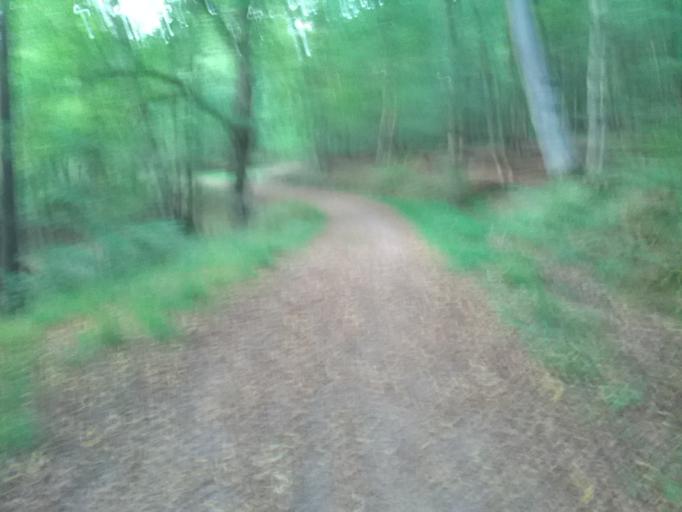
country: DE
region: Thuringia
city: Eisenach
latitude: 50.9529
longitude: 10.3114
